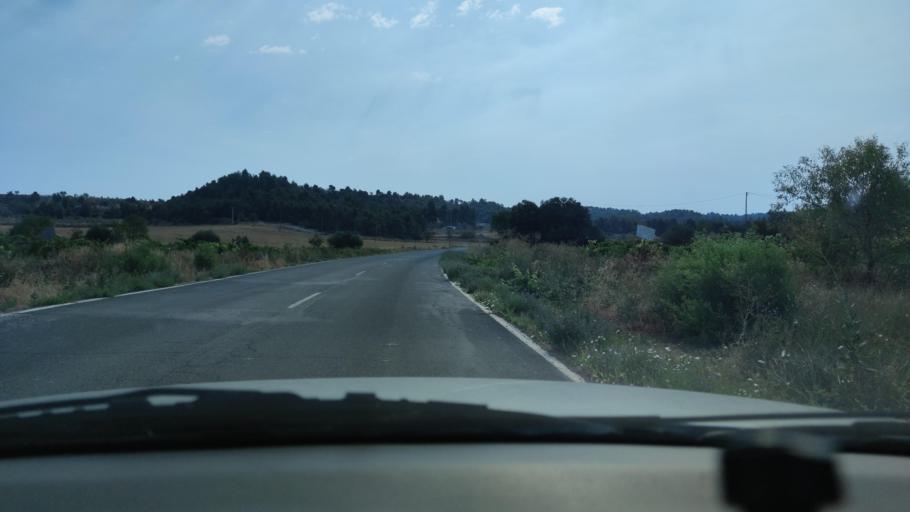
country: ES
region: Catalonia
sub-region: Provincia de Lleida
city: Fulleda
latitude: 41.5063
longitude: 0.9787
